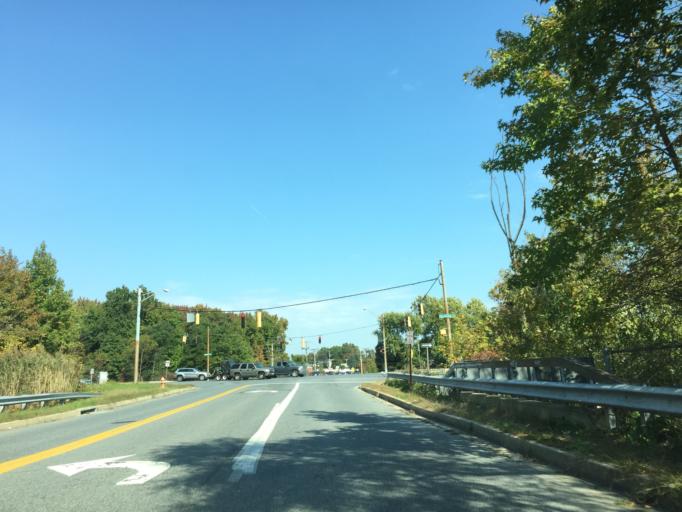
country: US
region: Maryland
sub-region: Baltimore County
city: Essex
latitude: 39.3105
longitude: -76.4531
